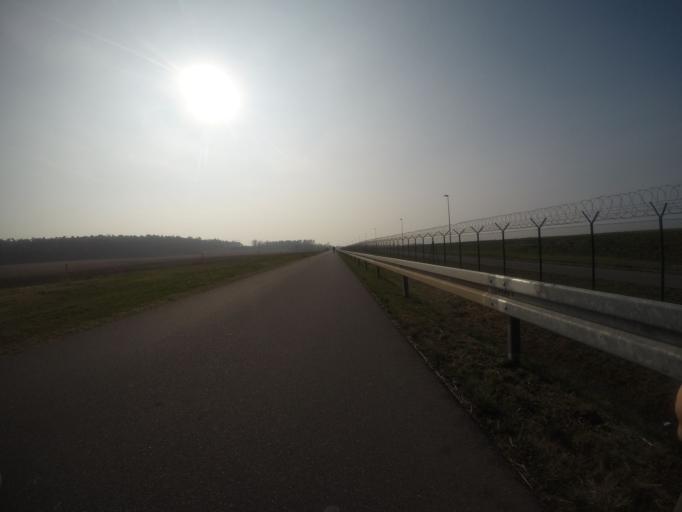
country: DE
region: Brandenburg
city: Schonefeld
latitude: 52.3436
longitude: 13.4732
